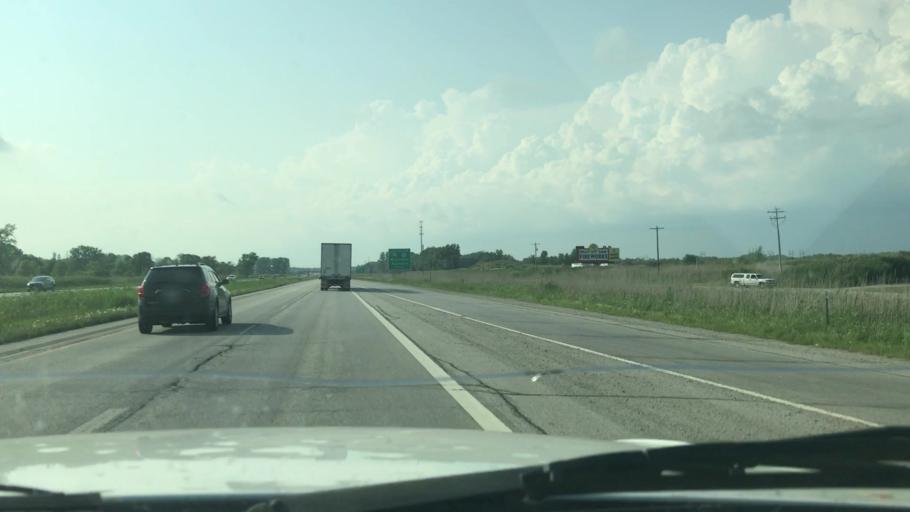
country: US
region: Wisconsin
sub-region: Brown County
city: Green Bay
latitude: 44.5438
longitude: -88.0305
